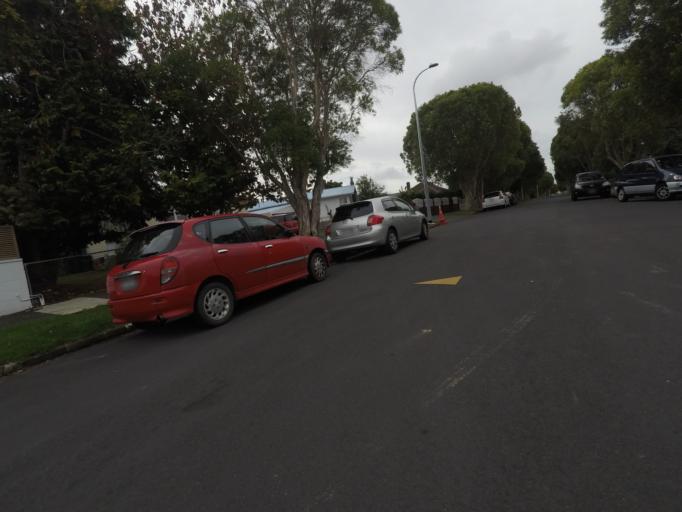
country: NZ
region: Auckland
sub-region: Auckland
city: Rosebank
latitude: -36.8915
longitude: 174.6789
